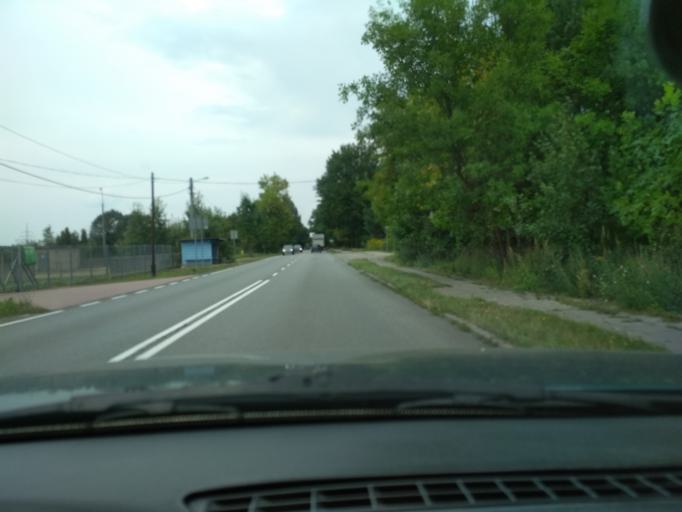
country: PL
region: Silesian Voivodeship
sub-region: Powiat zawiercianski
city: Wysoka
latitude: 50.4520
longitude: 19.3731
